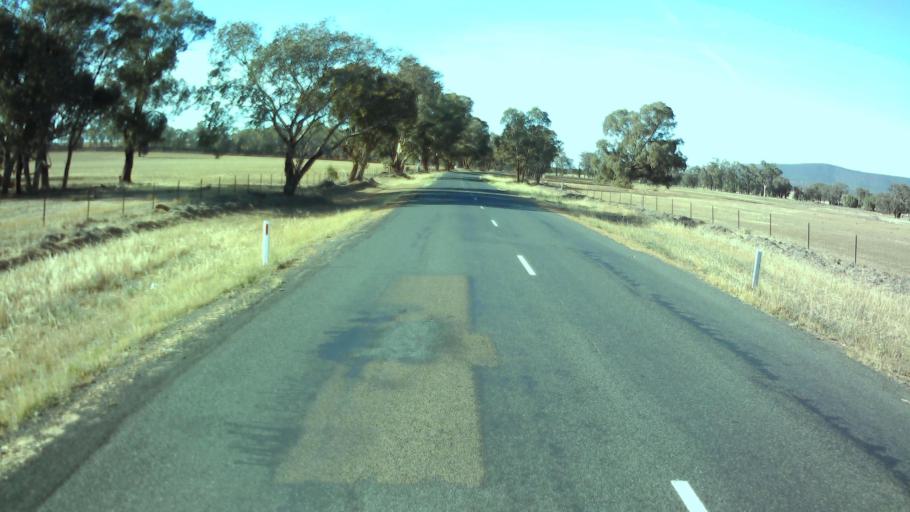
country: AU
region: New South Wales
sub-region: Weddin
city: Grenfell
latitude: -33.9369
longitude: 148.1375
